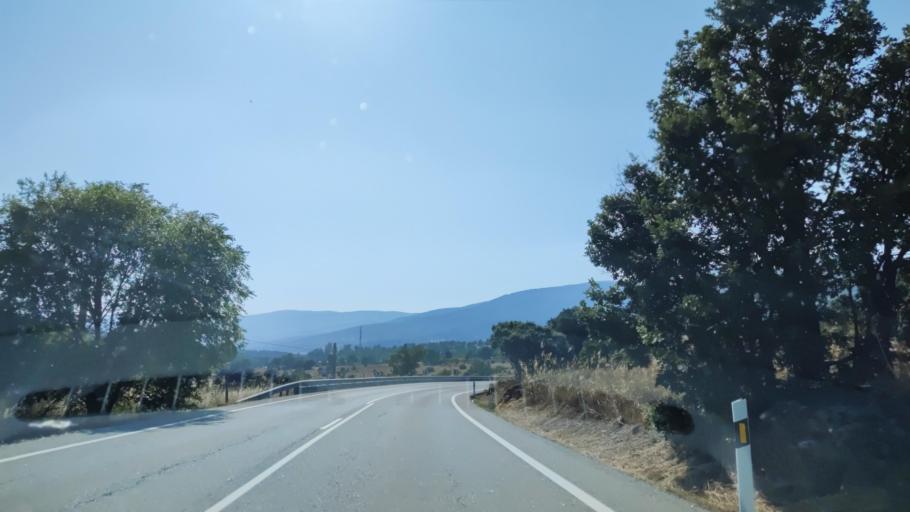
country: ES
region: Madrid
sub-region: Provincia de Madrid
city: Lozoya
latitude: 40.9468
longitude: -3.7598
